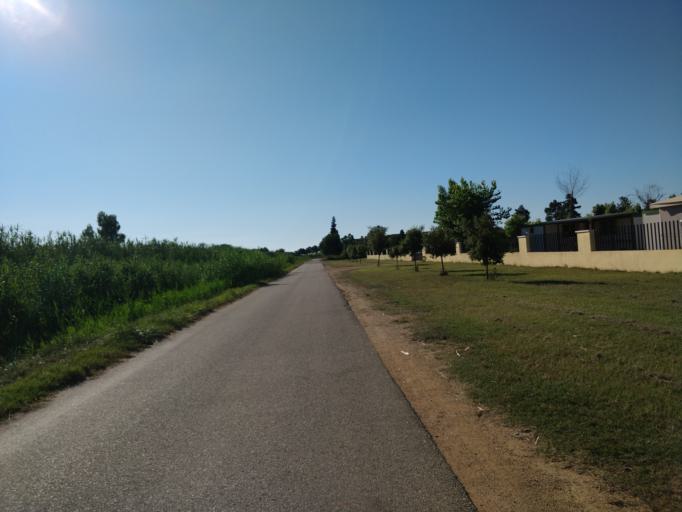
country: IT
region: Sardinia
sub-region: Provincia di Ogliastra
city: Lotzorai
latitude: 39.9608
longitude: 9.6784
